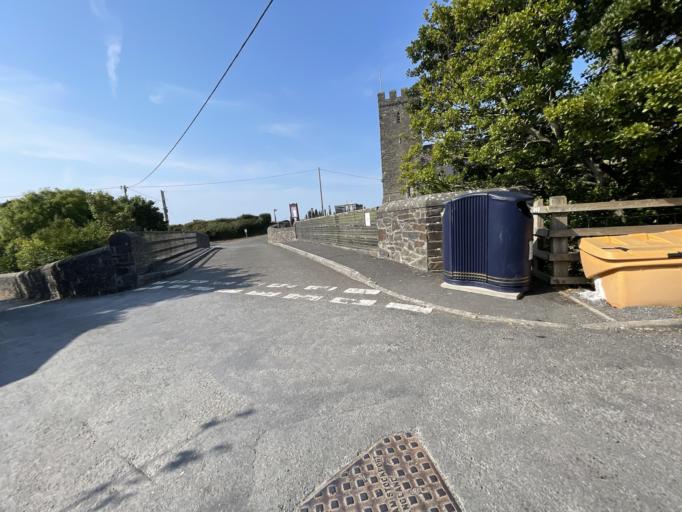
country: GB
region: Wales
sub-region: County of Ceredigion
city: Llanon
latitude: 52.2849
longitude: -4.1822
